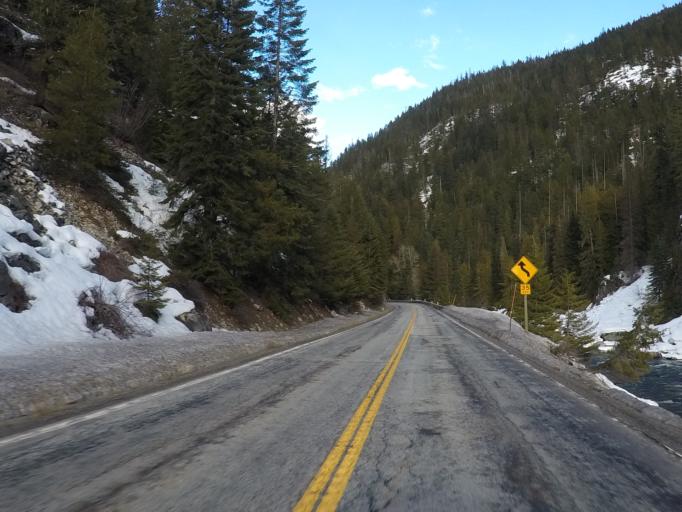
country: US
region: Montana
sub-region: Ravalli County
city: Hamilton
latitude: 46.5044
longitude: -114.8011
